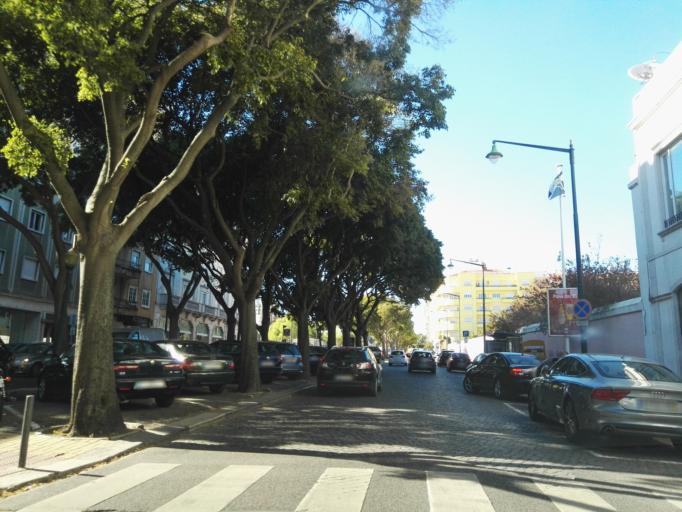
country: PT
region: Lisbon
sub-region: Lisbon
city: Lisbon
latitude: 38.7256
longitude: -9.1572
